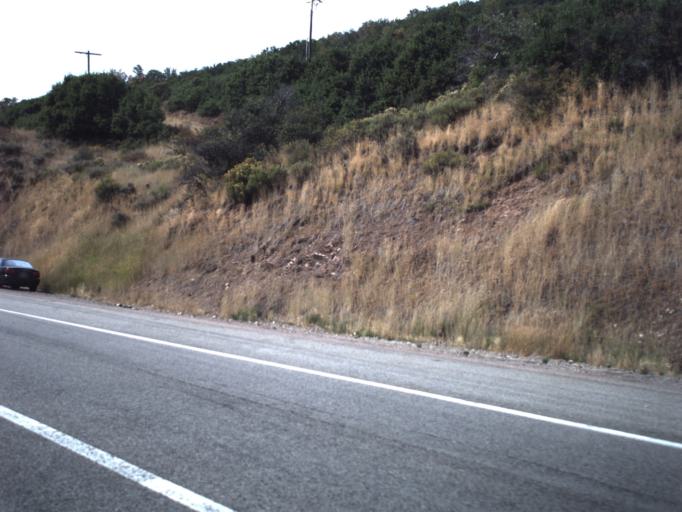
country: US
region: Utah
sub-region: Summit County
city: Summit Park
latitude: 40.7541
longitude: -111.6209
